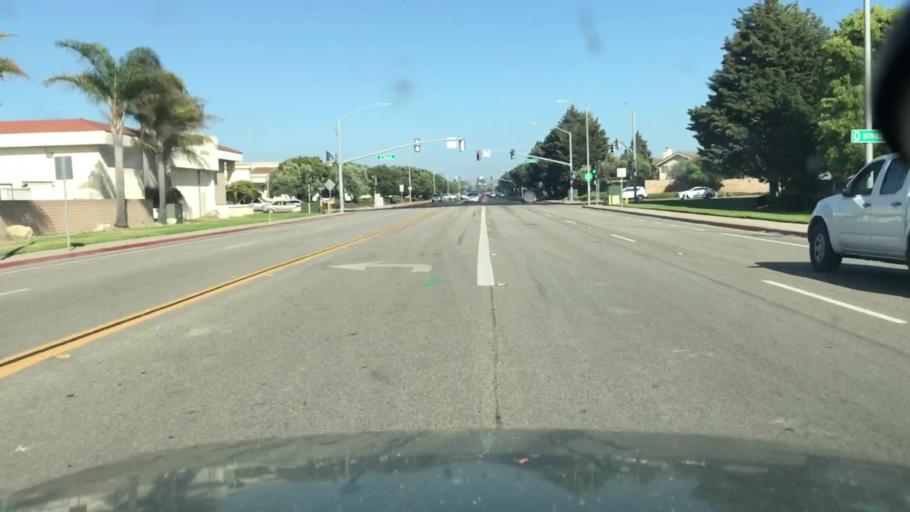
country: US
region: California
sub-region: Santa Barbara County
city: Lompoc
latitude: 34.6609
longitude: -120.4675
